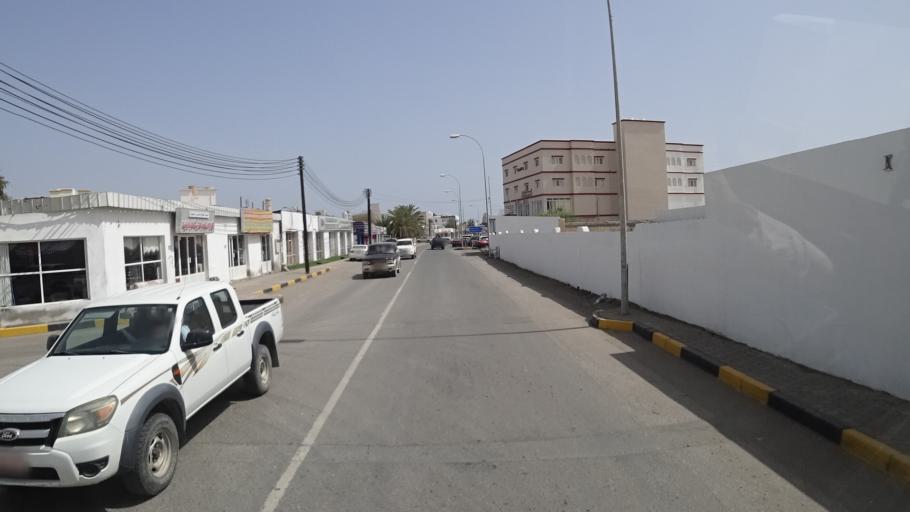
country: OM
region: Muhafazat Masqat
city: Muscat
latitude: 23.2581
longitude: 58.9136
